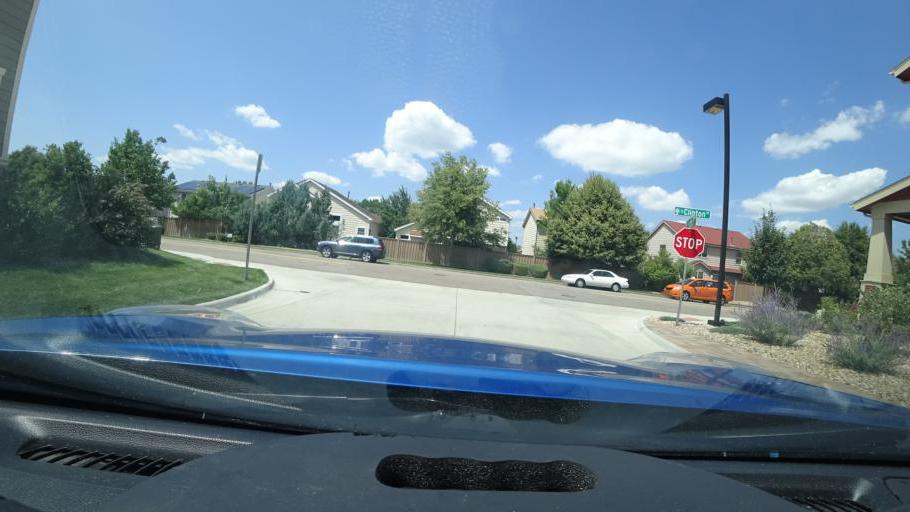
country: US
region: Colorado
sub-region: Arapahoe County
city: Glendale
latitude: 39.6938
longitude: -104.8774
